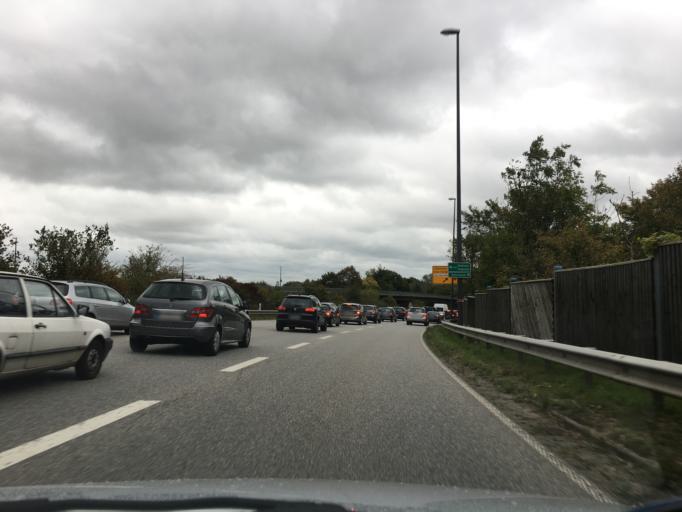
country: DE
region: Schleswig-Holstein
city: Altenholz
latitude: 54.3721
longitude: 10.1244
